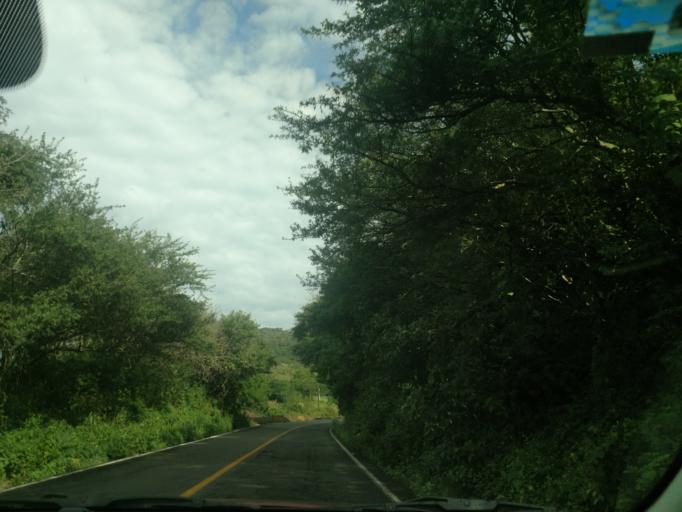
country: MX
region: Jalisco
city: Ameca
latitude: 20.5381
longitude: -104.1905
